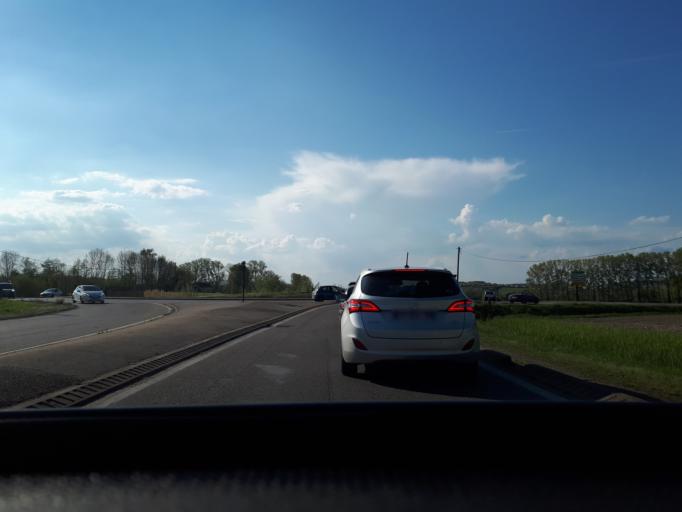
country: FR
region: Rhone-Alpes
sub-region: Departement de l'Isere
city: L'Isle-d'Abeau
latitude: 45.6071
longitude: 5.2540
